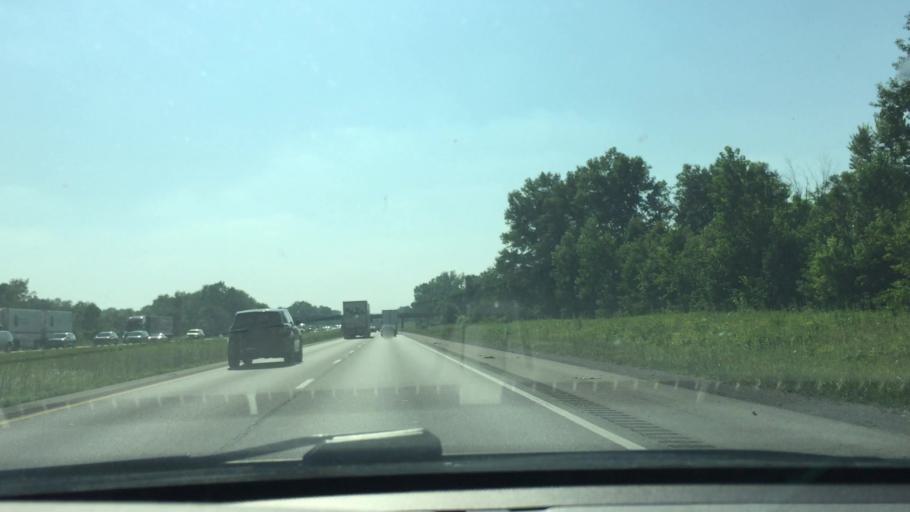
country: US
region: Ohio
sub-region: Licking County
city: Etna
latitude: 39.9511
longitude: -82.7256
